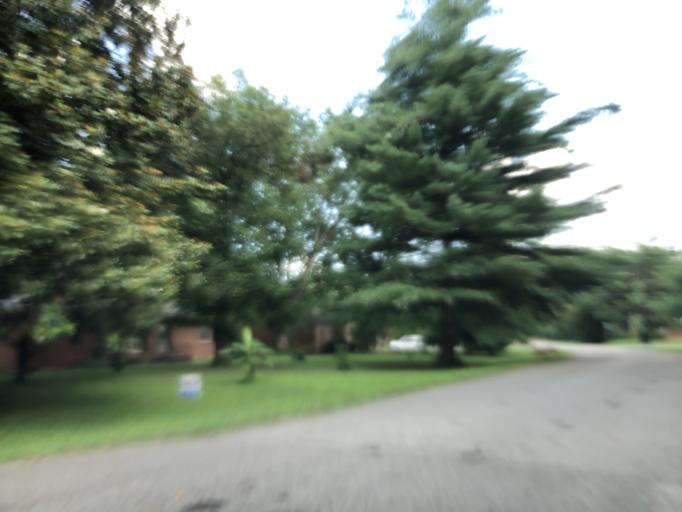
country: US
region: Tennessee
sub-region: Davidson County
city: Oak Hill
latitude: 36.1230
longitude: -86.7223
